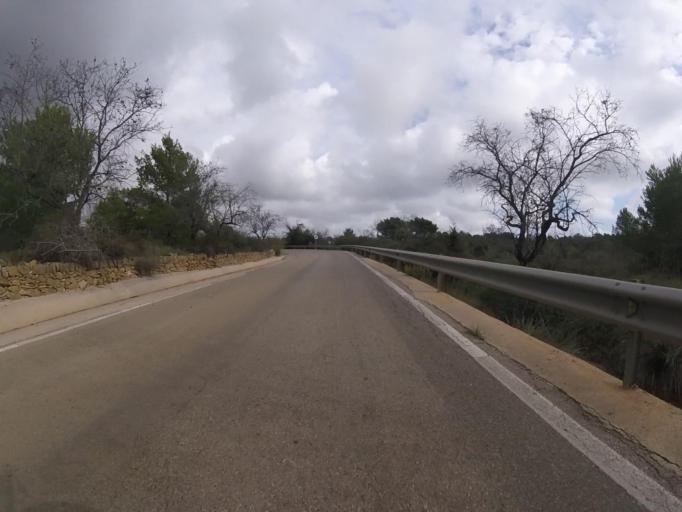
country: ES
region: Valencia
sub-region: Provincia de Castello
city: Cabanes
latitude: 40.1517
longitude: 0.0917
